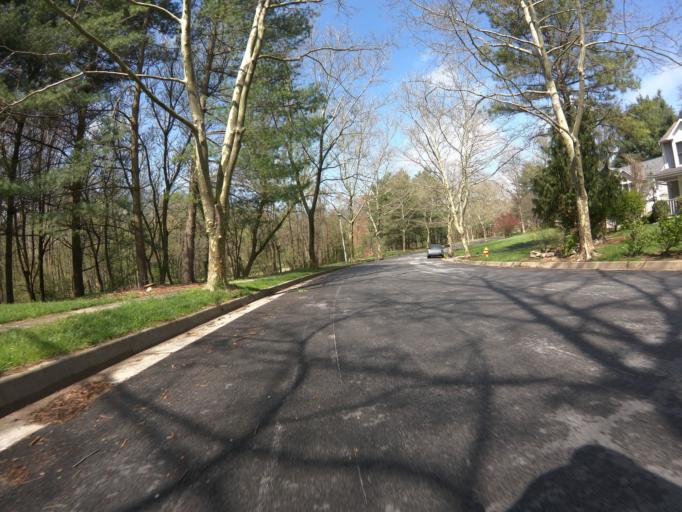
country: US
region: Maryland
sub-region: Howard County
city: Columbia
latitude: 39.2741
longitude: -76.8719
